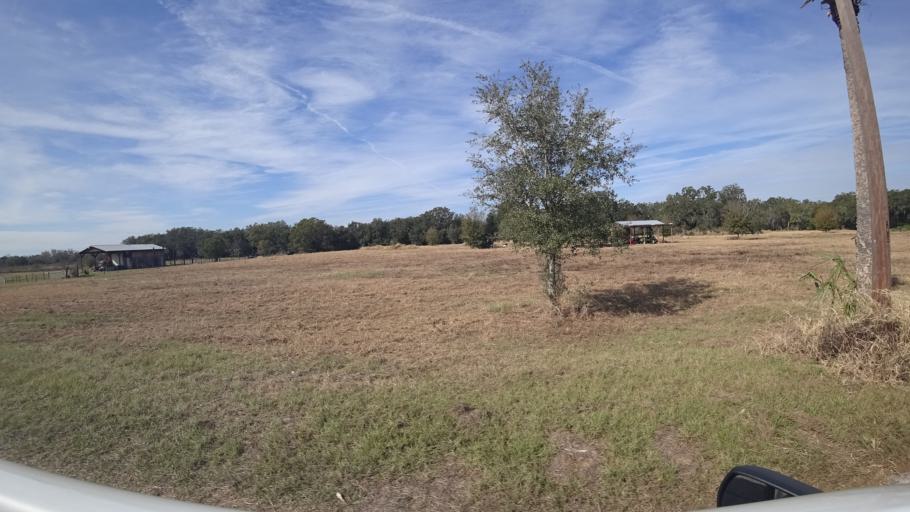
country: US
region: Florida
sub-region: Manatee County
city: Ellenton
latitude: 27.5855
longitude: -82.4277
